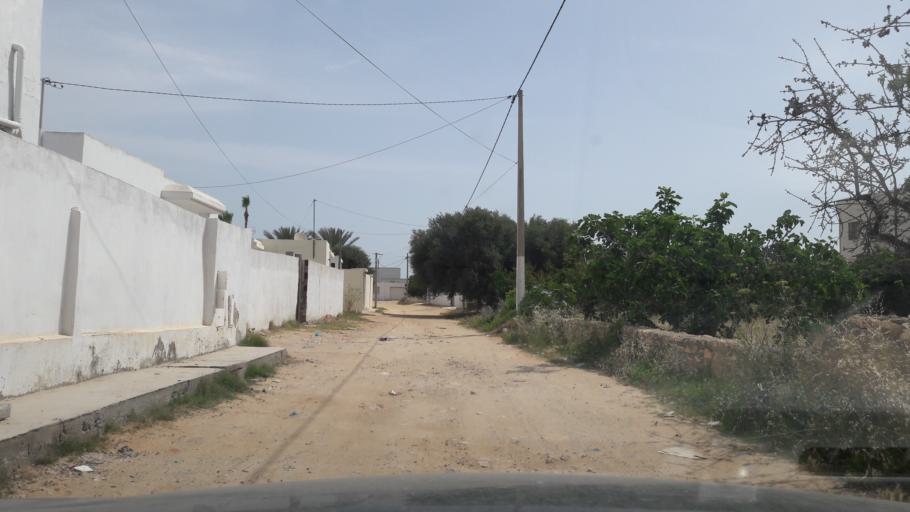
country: TN
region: Safaqis
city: Al Qarmadah
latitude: 34.7933
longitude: 10.7545
